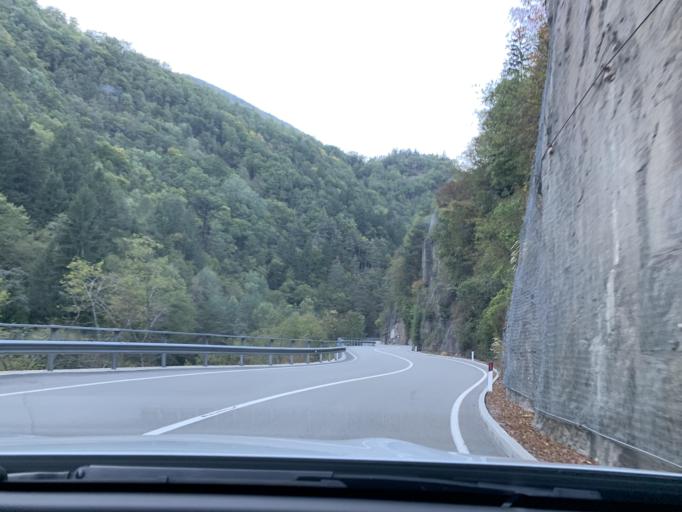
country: IT
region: Trentino-Alto Adige
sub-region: Bolzano
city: Cornedo All'Isarco
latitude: 46.4656
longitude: 11.4107
